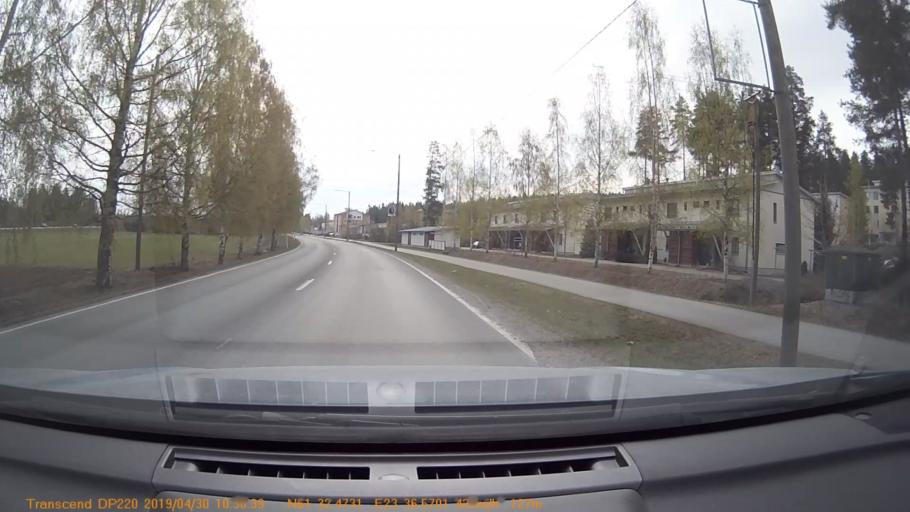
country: FI
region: Pirkanmaa
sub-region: Tampere
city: Yloejaervi
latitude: 61.5413
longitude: 23.6093
